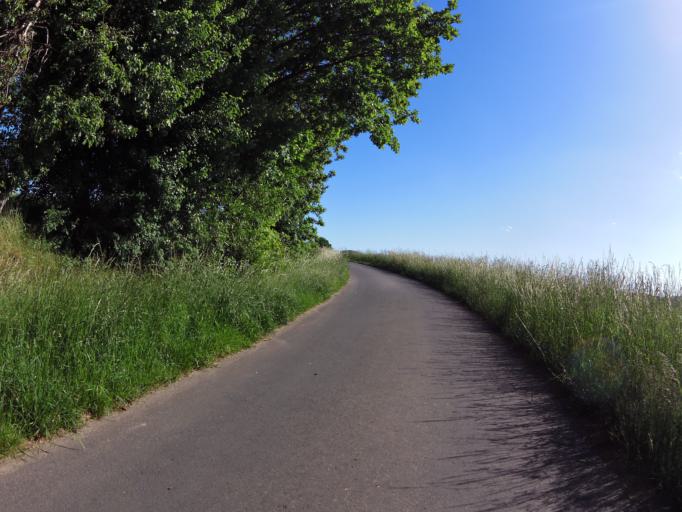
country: DE
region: Hesse
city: Philippsthal
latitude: 50.8349
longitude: 9.9995
